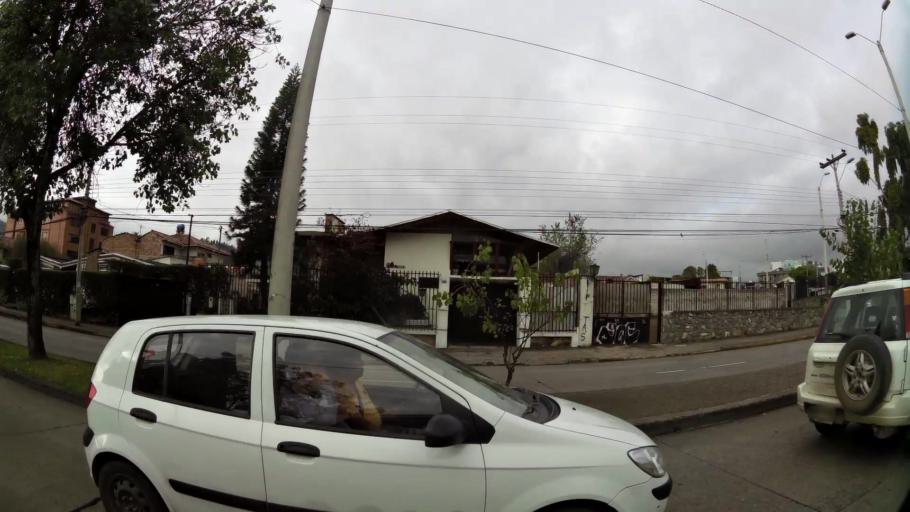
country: EC
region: Azuay
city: Cuenca
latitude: -2.9088
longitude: -79.0045
